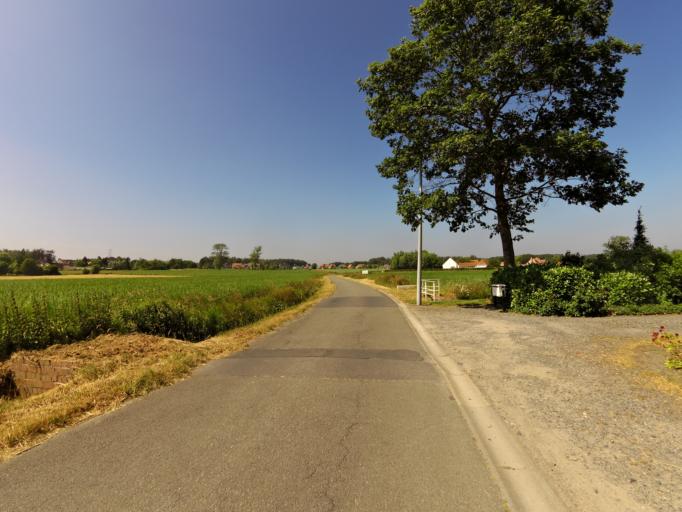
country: BE
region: Flanders
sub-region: Provincie West-Vlaanderen
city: Zedelgem
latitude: 51.1483
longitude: 3.1356
